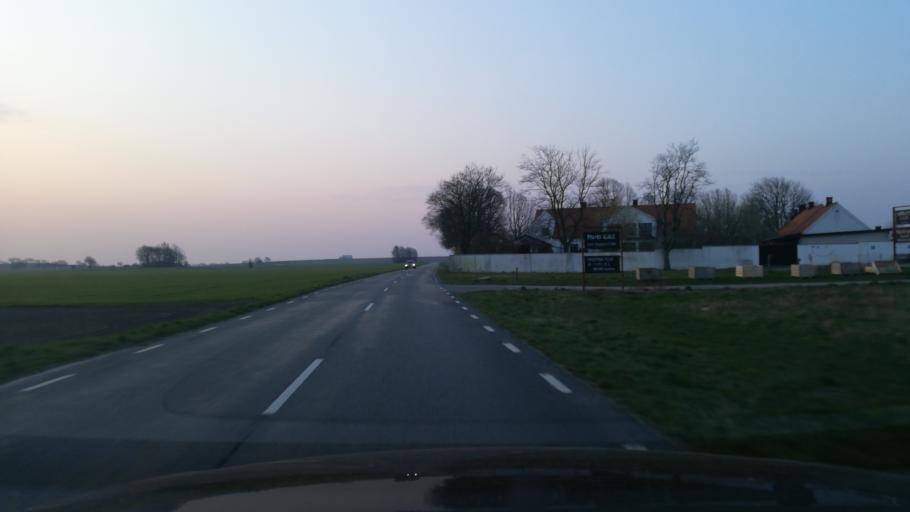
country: SE
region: Skane
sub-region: Ystads Kommun
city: Kopingebro
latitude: 55.4543
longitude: 14.1136
